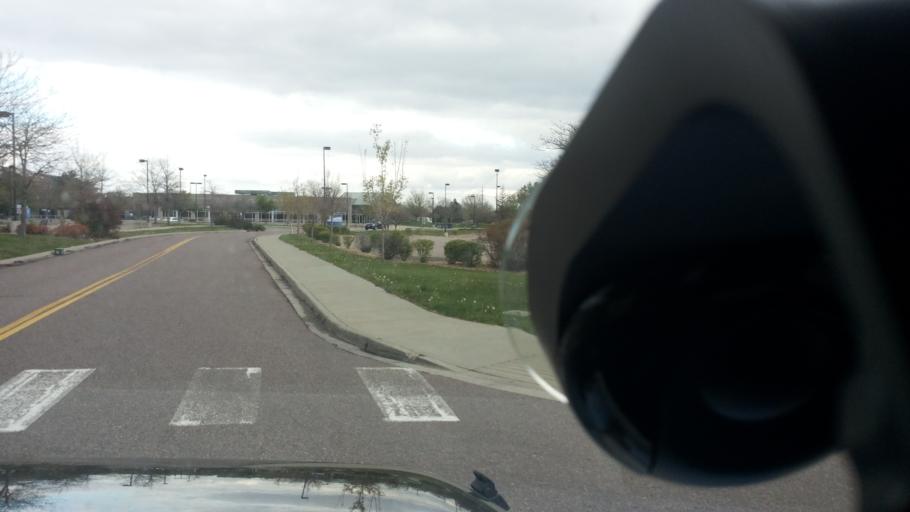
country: US
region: Colorado
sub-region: Boulder County
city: Superior
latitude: 39.9615
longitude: -105.1624
